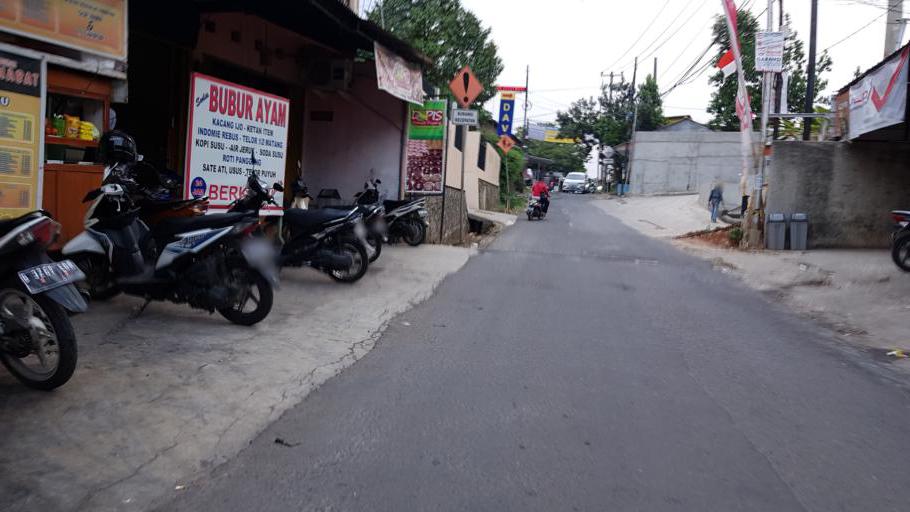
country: ID
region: West Java
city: Depok
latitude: -6.3691
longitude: 106.8172
